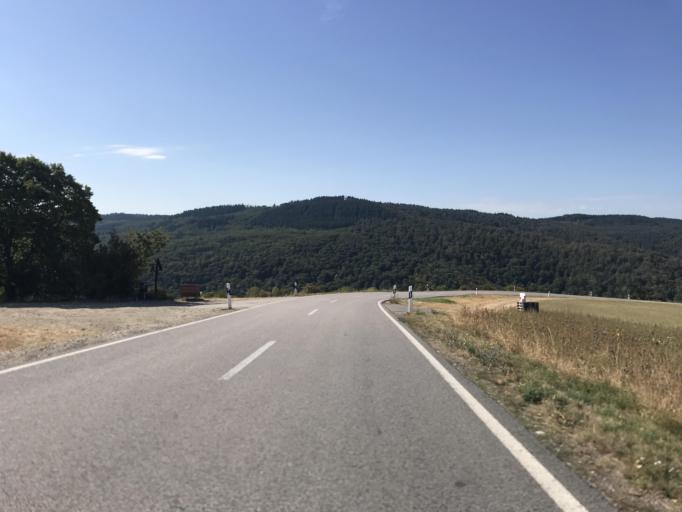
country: DE
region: Rheinland-Pfalz
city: Trechtingshausen
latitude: 50.0499
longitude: 7.8842
